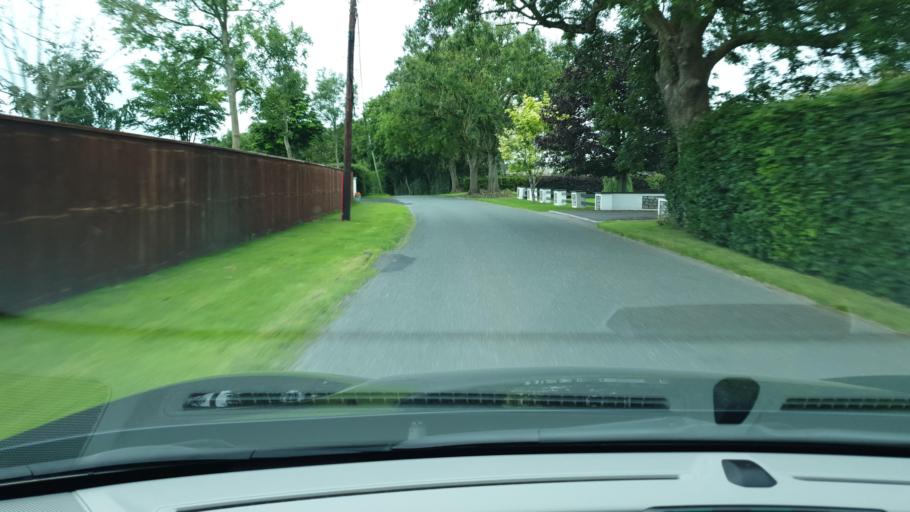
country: IE
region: Leinster
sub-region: An Mhi
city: Dunboyne
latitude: 53.4380
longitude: -6.4866
